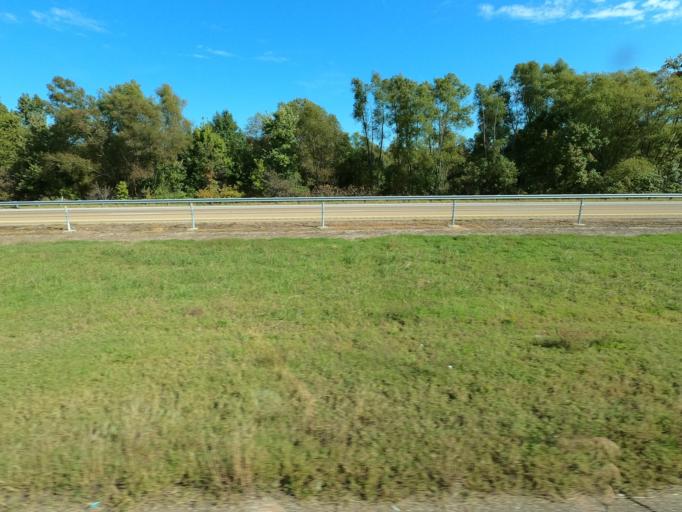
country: US
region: Tennessee
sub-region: Shelby County
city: Millington
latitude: 35.3124
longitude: -89.8617
